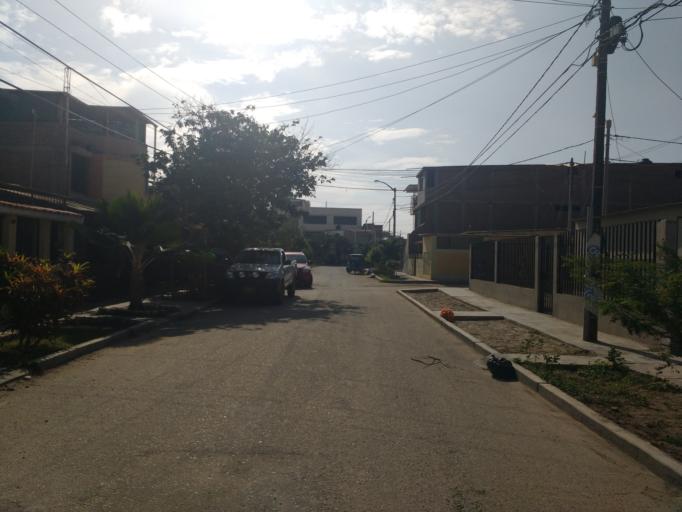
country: PE
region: Piura
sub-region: Provincia de Piura
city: Piura
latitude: -5.1916
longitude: -80.6453
